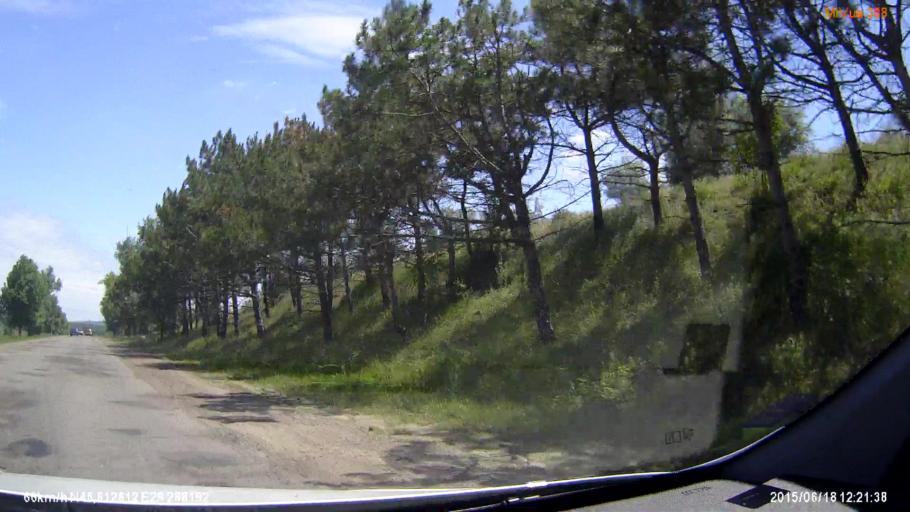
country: MD
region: Causeni
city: Causeni
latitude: 46.6126
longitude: 29.2877
